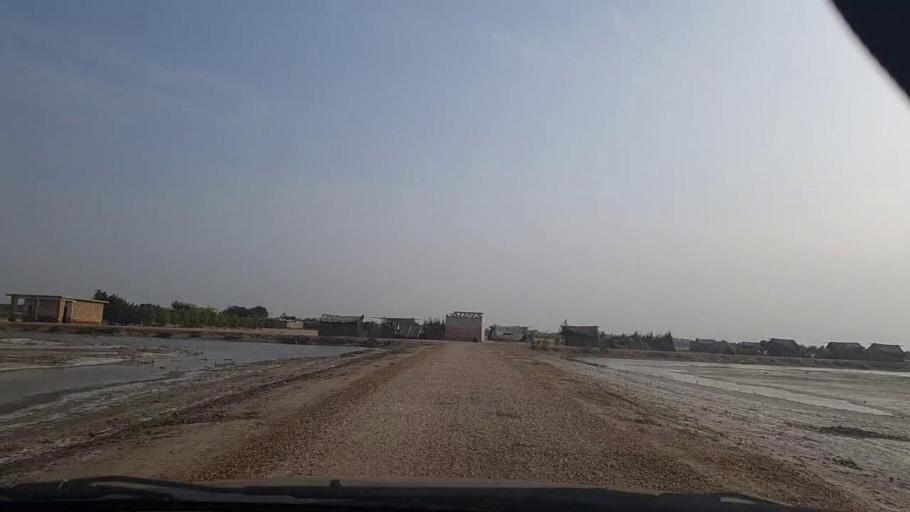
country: PK
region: Sindh
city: Thatta
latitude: 24.7237
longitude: 67.9026
